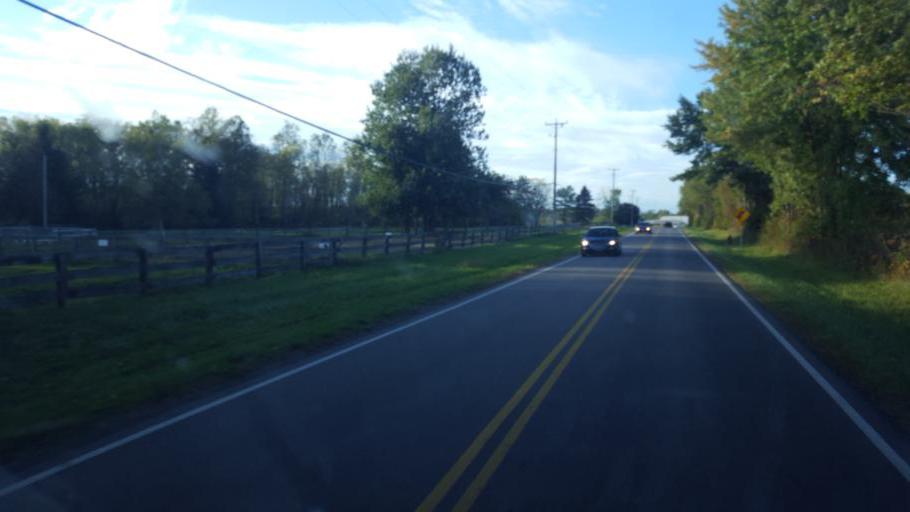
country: US
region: Ohio
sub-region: Licking County
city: Pataskala
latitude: 40.0242
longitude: -82.7304
